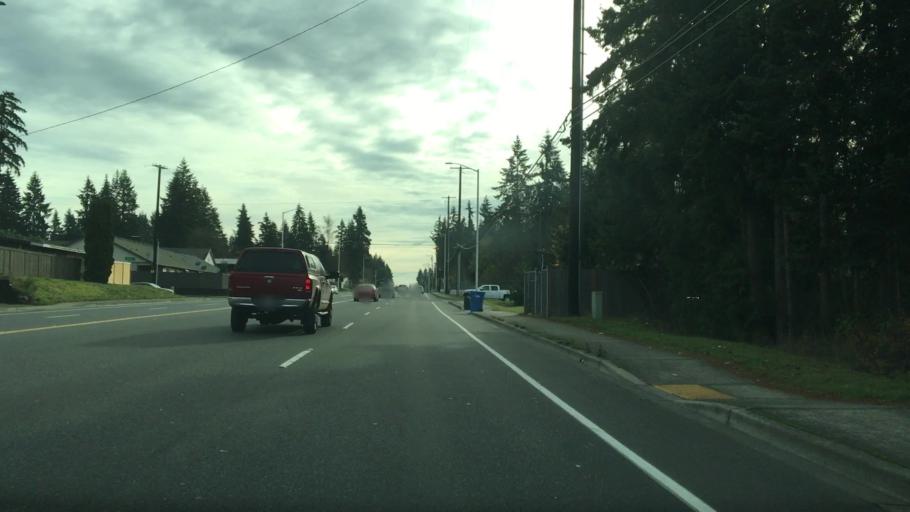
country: US
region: Washington
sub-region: Pierce County
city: South Hill
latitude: 47.1501
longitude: -122.3040
